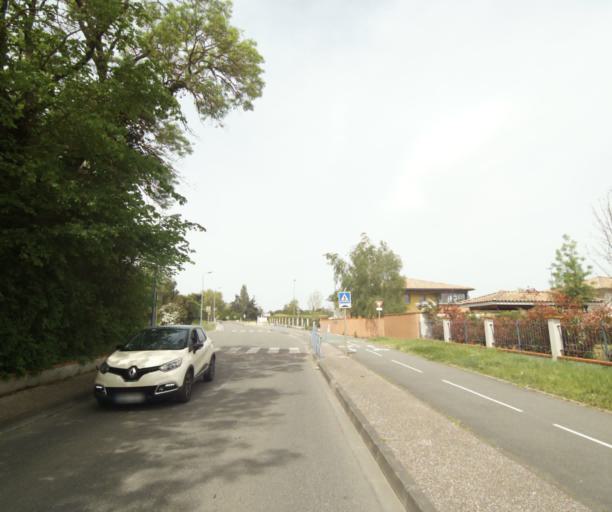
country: FR
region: Midi-Pyrenees
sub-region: Departement de la Haute-Garonne
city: Auzeville-Tolosane
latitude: 43.5226
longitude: 1.4901
